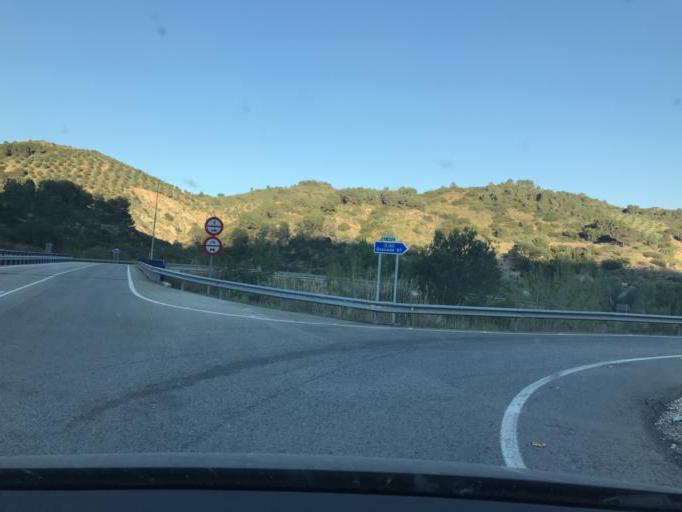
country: ES
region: Andalusia
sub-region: Provincia de Jaen
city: Cambil
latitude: 37.6755
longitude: -3.6253
